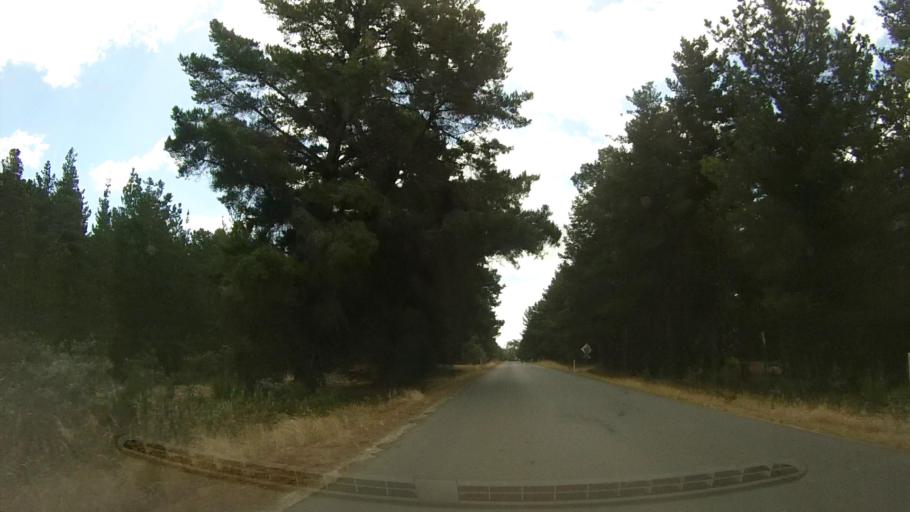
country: AU
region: Tasmania
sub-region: Clarence
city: Seven Mile Beach
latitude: -42.8364
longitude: 147.5253
